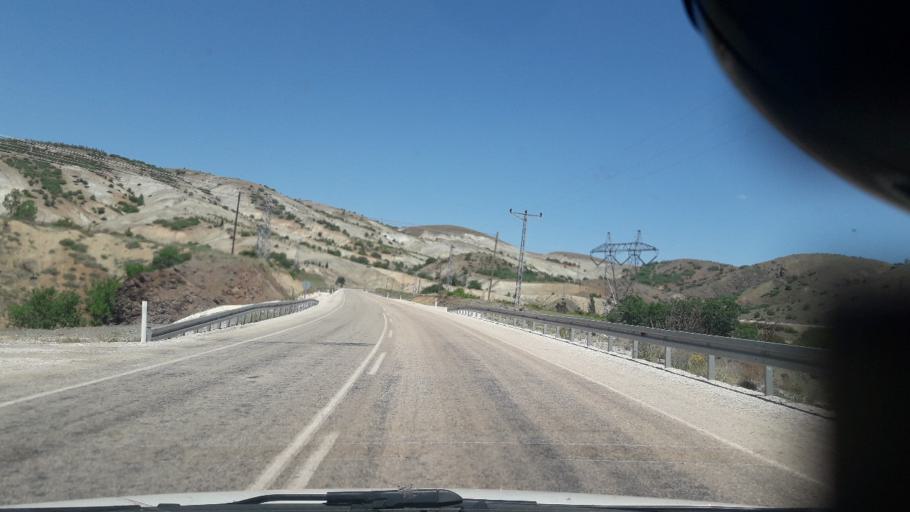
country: TR
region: Malatya
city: Hekimhan
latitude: 38.8278
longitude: 37.8613
